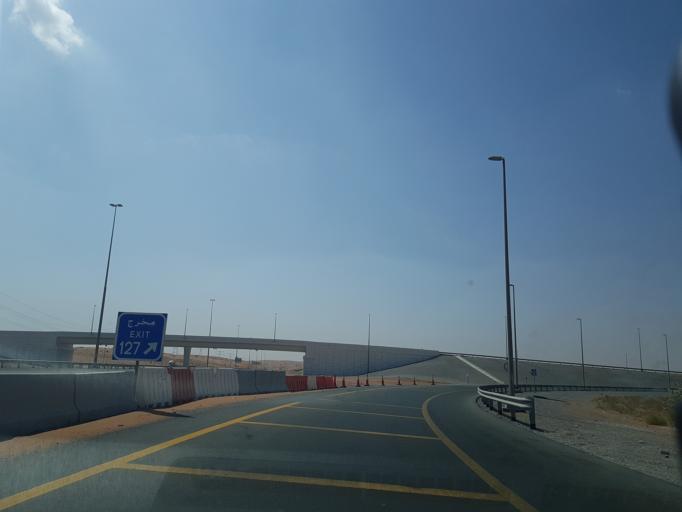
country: AE
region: Ra's al Khaymah
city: Ras al-Khaimah
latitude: 25.6674
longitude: 55.8958
